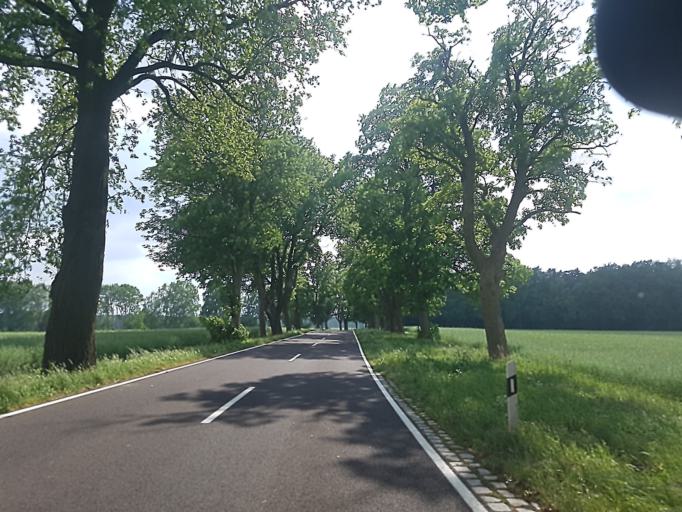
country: DE
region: Brandenburg
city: Gorzke
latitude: 52.0629
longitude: 12.2944
